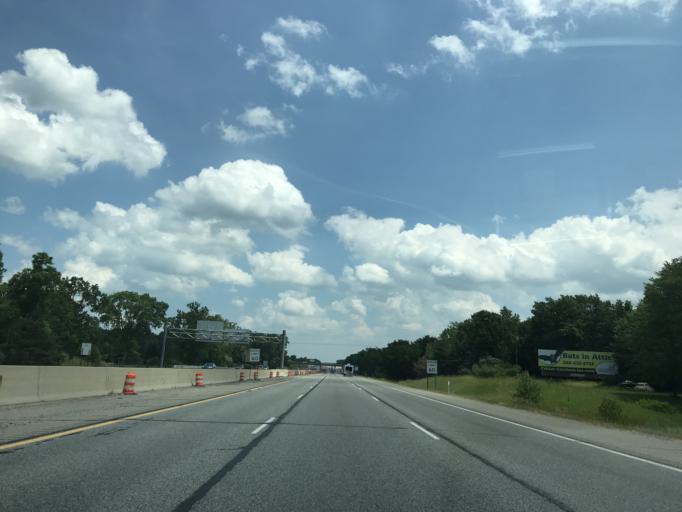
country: US
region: Michigan
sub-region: Livingston County
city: Brighton
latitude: 42.5221
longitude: -83.7270
